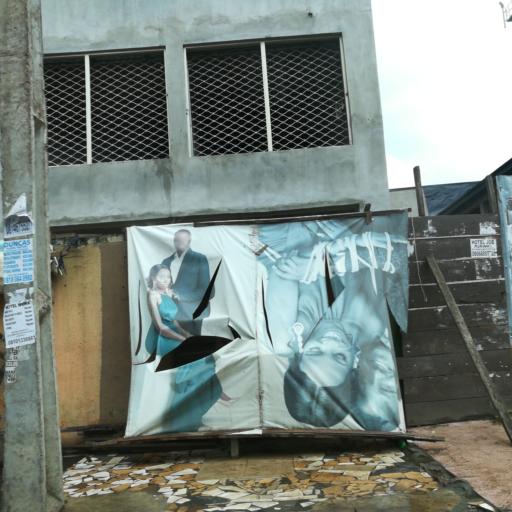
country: NG
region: Lagos
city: Agege
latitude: 6.5986
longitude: 3.2930
